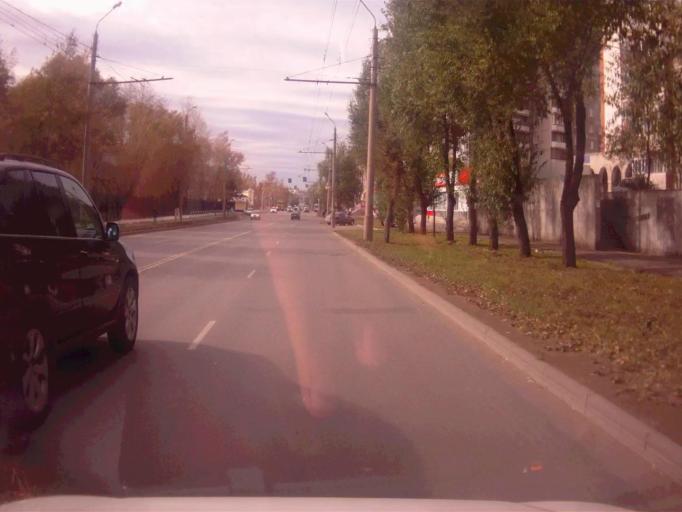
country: RU
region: Chelyabinsk
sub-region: Gorod Chelyabinsk
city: Chelyabinsk
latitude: 55.1130
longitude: 61.4610
